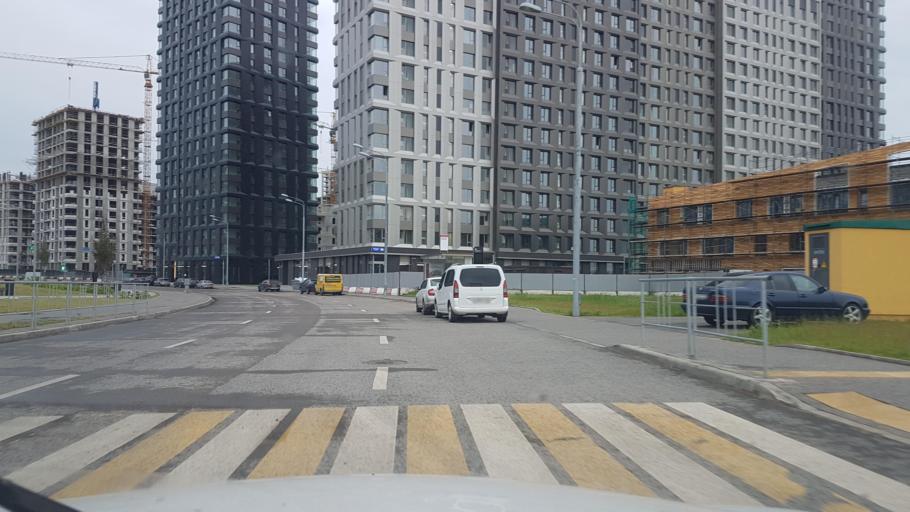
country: RU
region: Moscow
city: Strogino
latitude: 55.8217
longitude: 37.4235
